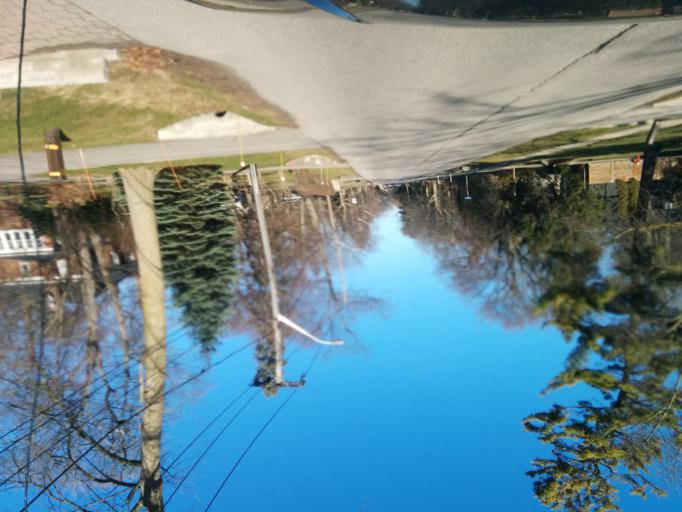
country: CA
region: Ontario
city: Mississauga
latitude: 43.5582
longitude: -79.5945
